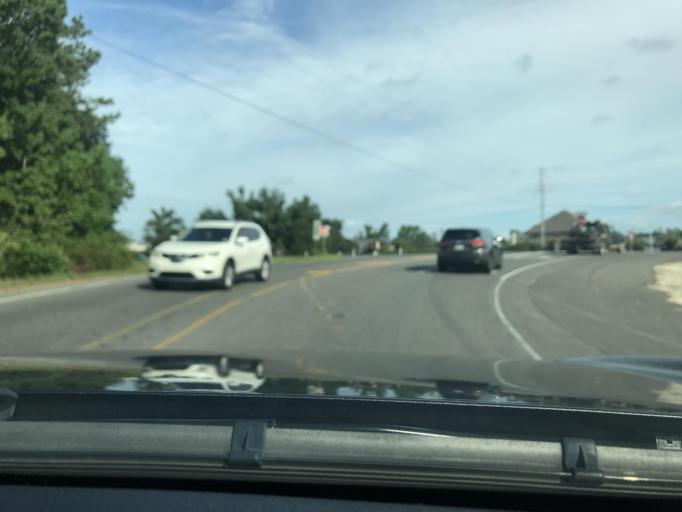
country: US
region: Louisiana
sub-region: Calcasieu Parish
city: Moss Bluff
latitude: 30.3011
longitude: -93.2448
